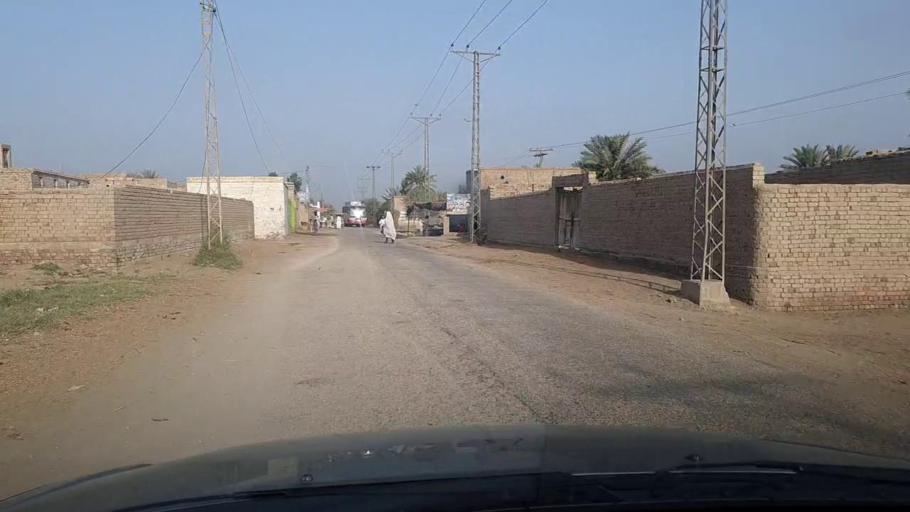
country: PK
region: Sindh
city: Pir jo Goth
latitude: 27.5703
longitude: 68.6290
